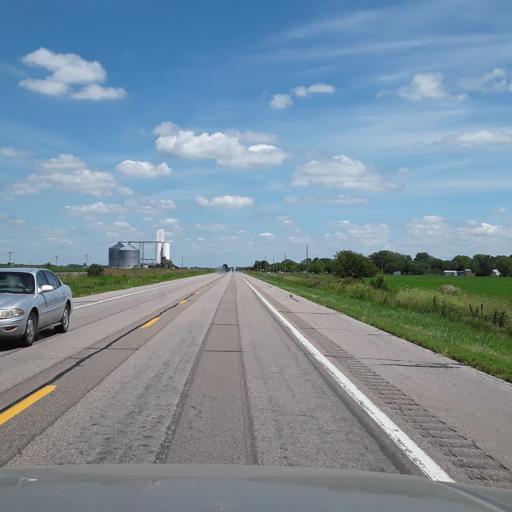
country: US
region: Nebraska
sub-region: Nance County
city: Genoa
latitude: 41.3231
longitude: -97.6464
